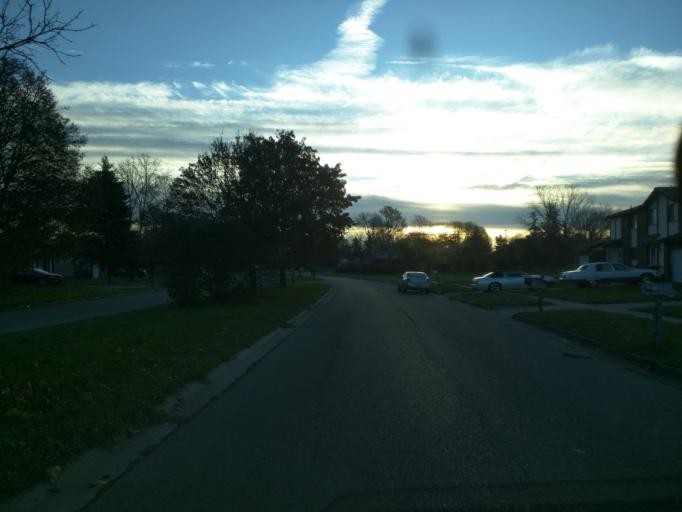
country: US
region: Michigan
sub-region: Eaton County
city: Waverly
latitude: 42.6892
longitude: -84.6054
